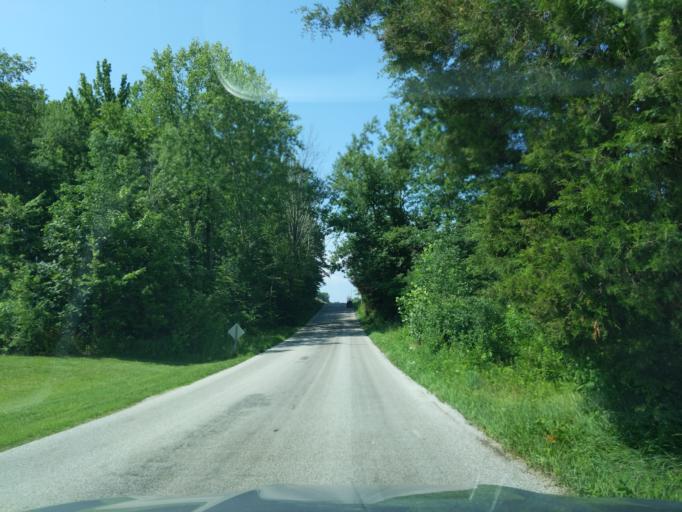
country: US
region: Indiana
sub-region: Ripley County
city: Osgood
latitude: 39.1345
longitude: -85.3404
